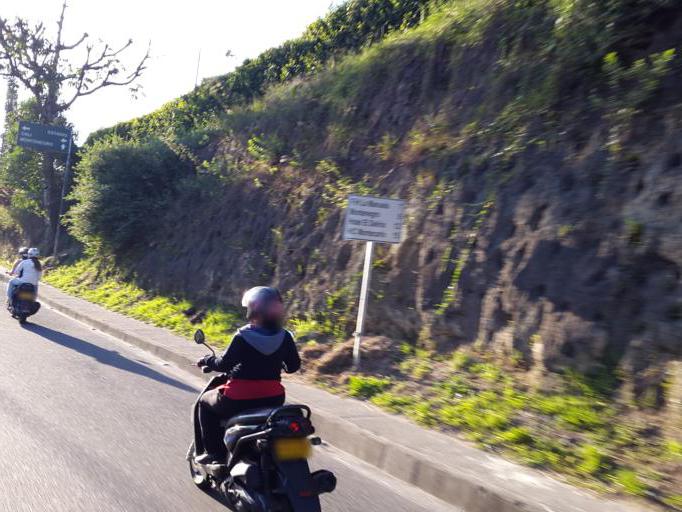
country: CO
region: Quindio
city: Armenia
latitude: 4.5315
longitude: -75.6993
